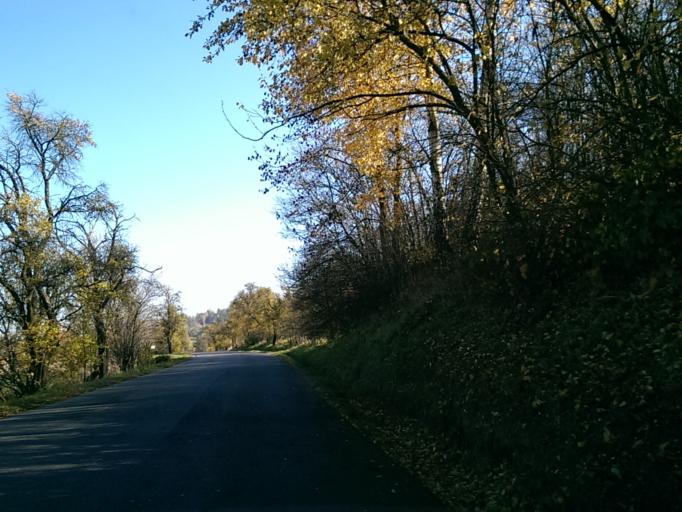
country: CZ
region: Liberecky
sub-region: Okres Semily
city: Turnov
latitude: 50.5684
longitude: 15.1347
